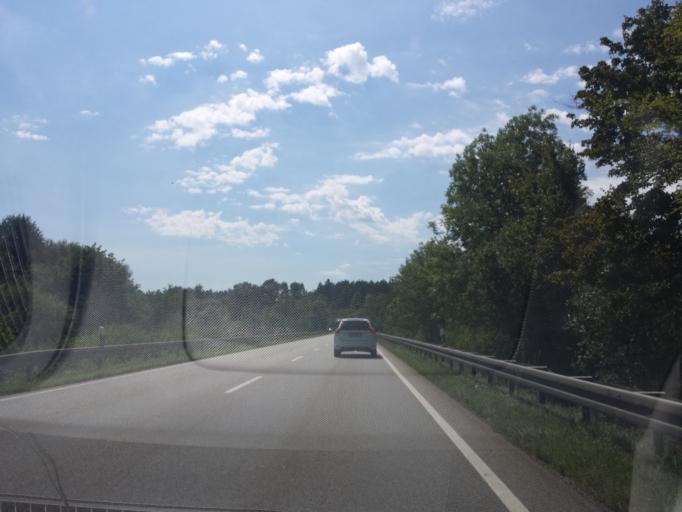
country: DE
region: Bavaria
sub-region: Lower Bavaria
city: Rattiszell
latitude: 49.0241
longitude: 12.6497
